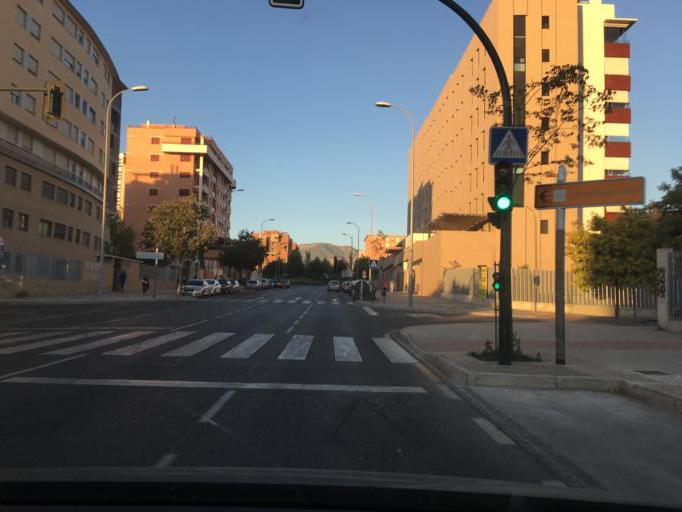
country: ES
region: Andalusia
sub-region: Provincia de Granada
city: Granada
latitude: 37.1983
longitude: -3.6192
